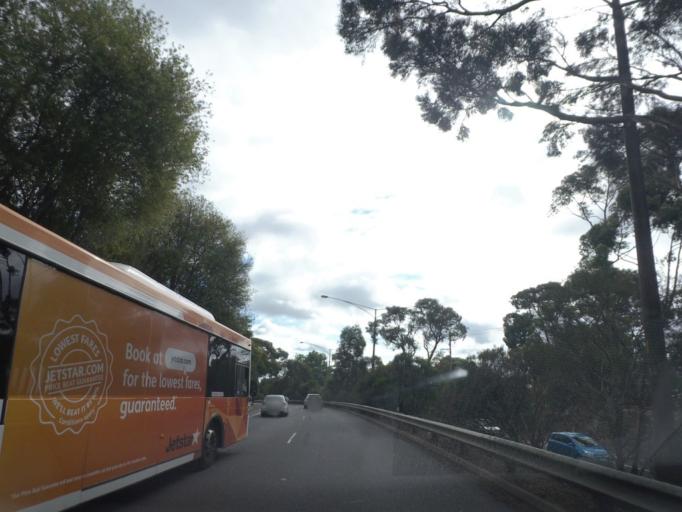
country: AU
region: Victoria
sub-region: Maroondah
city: Heathmont
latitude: -37.8257
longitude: 145.2488
